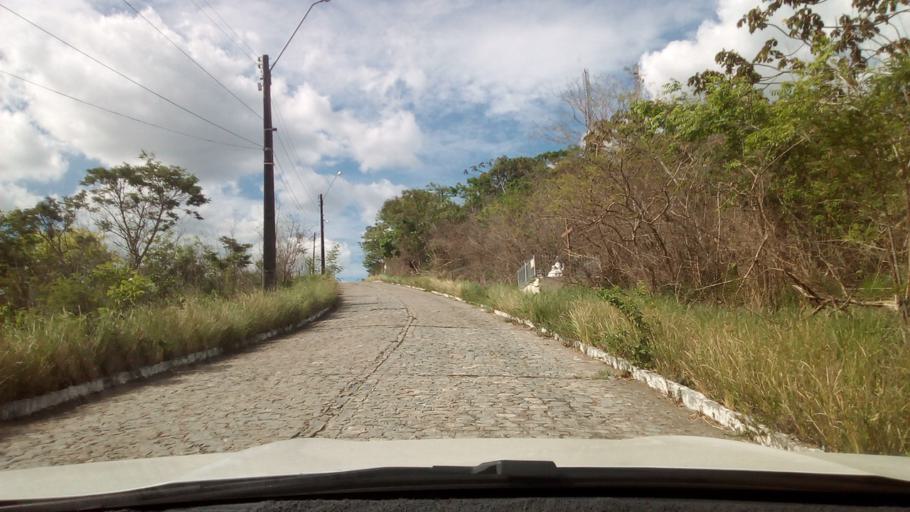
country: BR
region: Paraiba
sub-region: Guarabira
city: Guarabira
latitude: -6.8328
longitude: -35.4968
